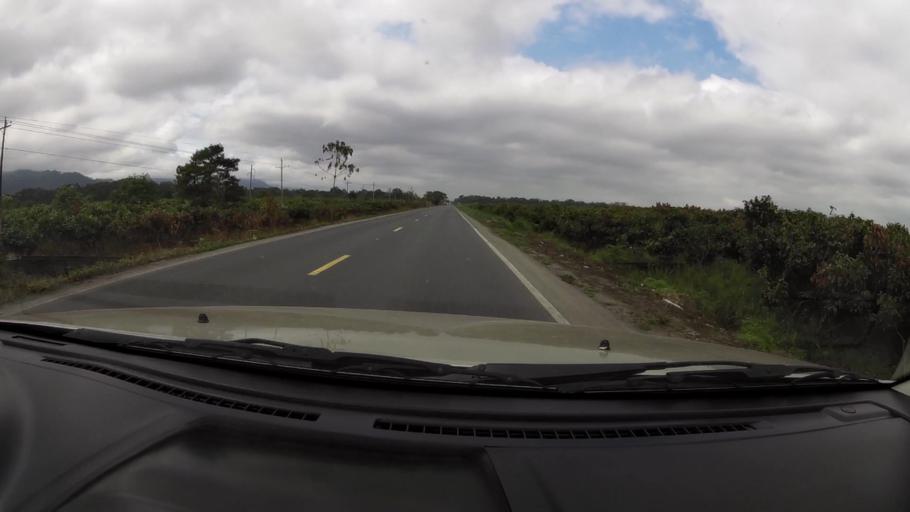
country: EC
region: Guayas
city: Naranjal
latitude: -2.6936
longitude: -79.6441
